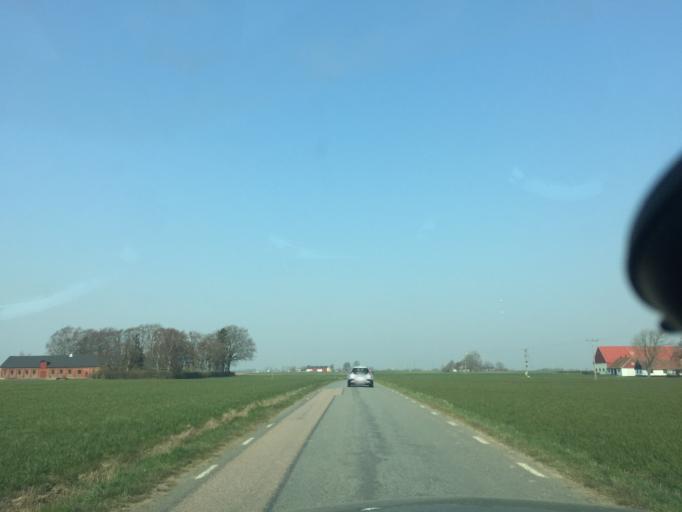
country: SE
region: Skane
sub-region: Simrishamns Kommun
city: Simrishamn
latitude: 55.4514
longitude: 14.2158
